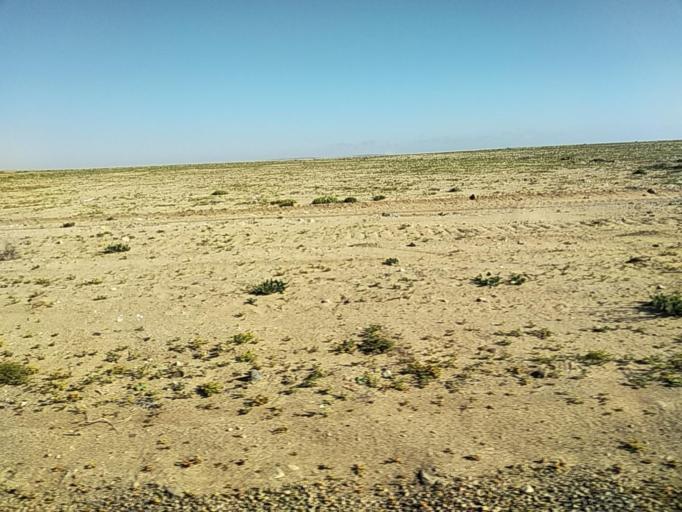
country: CL
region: Atacama
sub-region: Provincia de Copiapo
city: Copiapo
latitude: -27.3161
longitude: -70.8755
